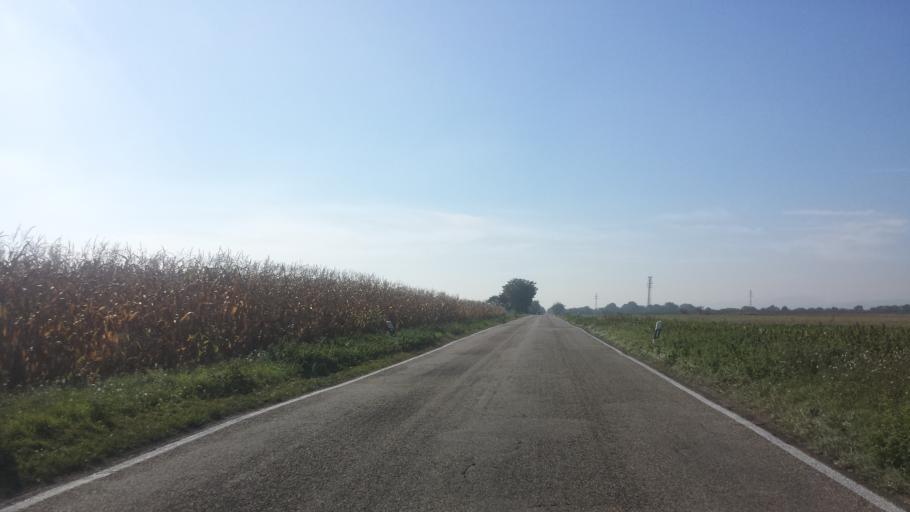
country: DE
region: Rheinland-Pfalz
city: Insheim
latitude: 49.1696
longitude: 8.1649
